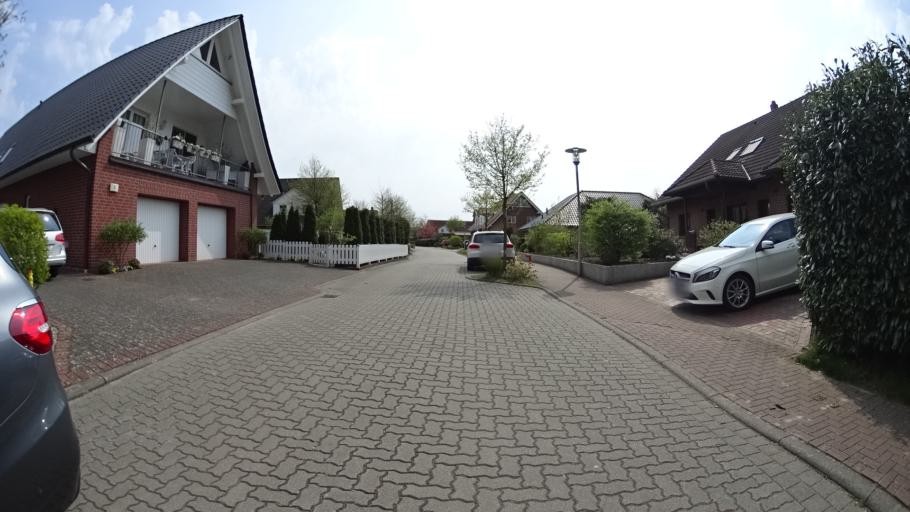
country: DE
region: Lower Saxony
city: Jork
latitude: 53.5391
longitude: 9.6925
